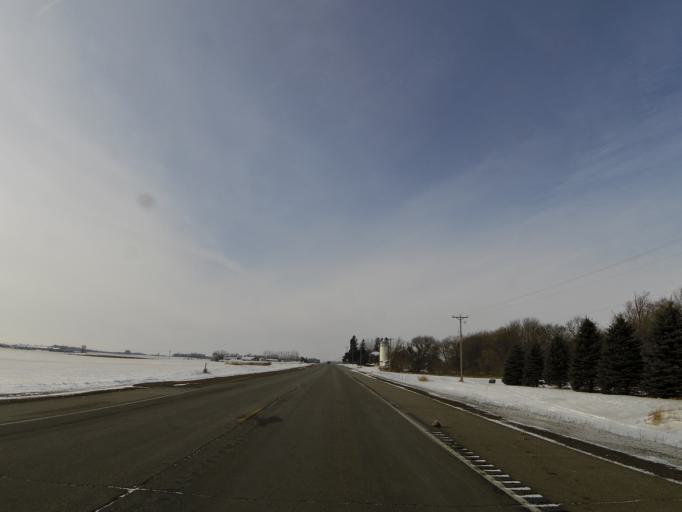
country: US
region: Minnesota
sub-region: McLeod County
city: Lester Prairie
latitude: 44.9063
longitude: -94.0886
